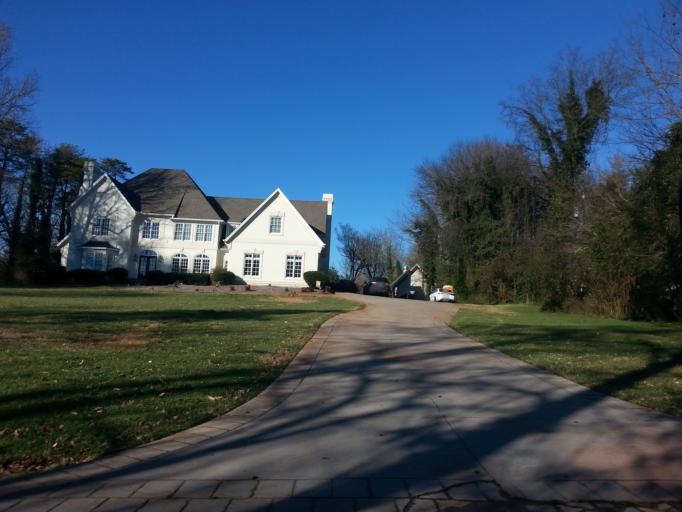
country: US
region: Tennessee
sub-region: Knox County
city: Knoxville
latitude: 35.8902
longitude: -83.9784
